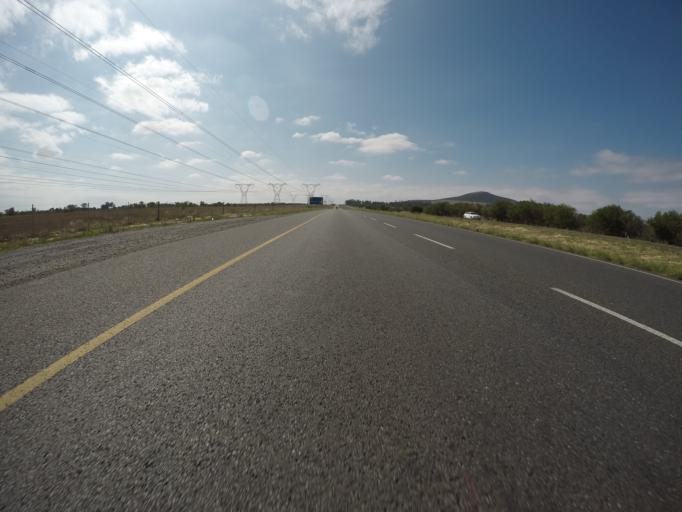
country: ZA
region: Western Cape
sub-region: City of Cape Town
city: Sunset Beach
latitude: -33.7402
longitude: 18.5455
